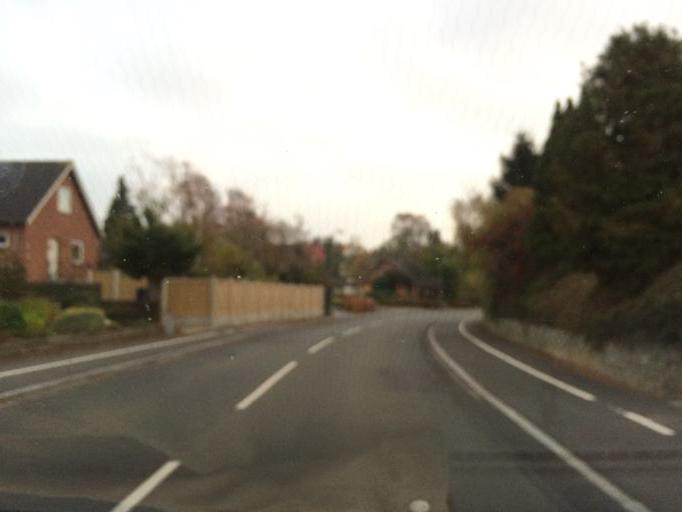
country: DK
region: Central Jutland
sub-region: Silkeborg Kommune
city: Silkeborg
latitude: 56.1834
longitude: 9.5223
